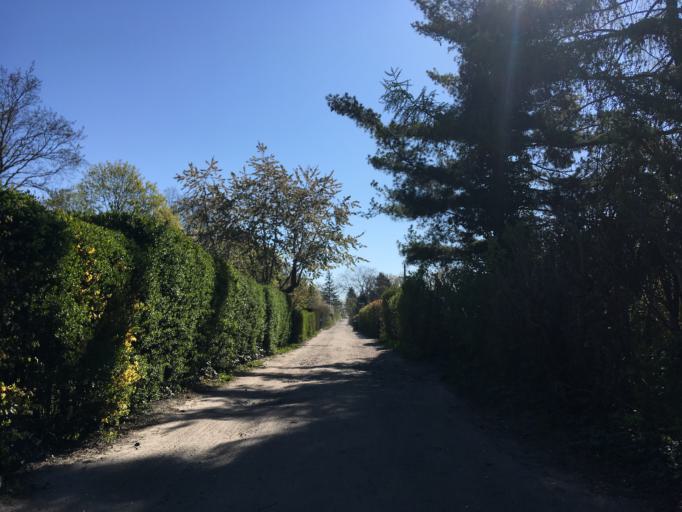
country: DE
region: Berlin
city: Blankenfelde
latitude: 52.6030
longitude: 13.3939
